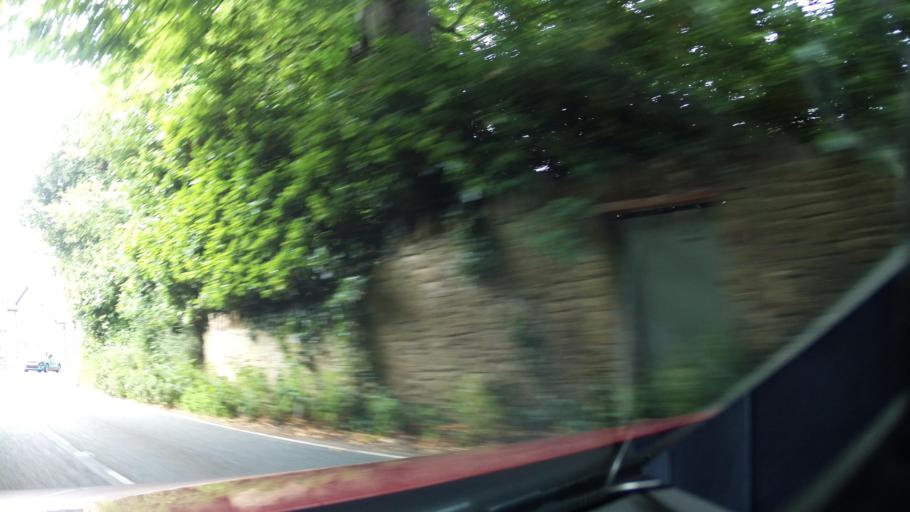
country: GB
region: England
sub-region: Somerset
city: Crewkerne
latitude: 50.8935
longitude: -2.7523
